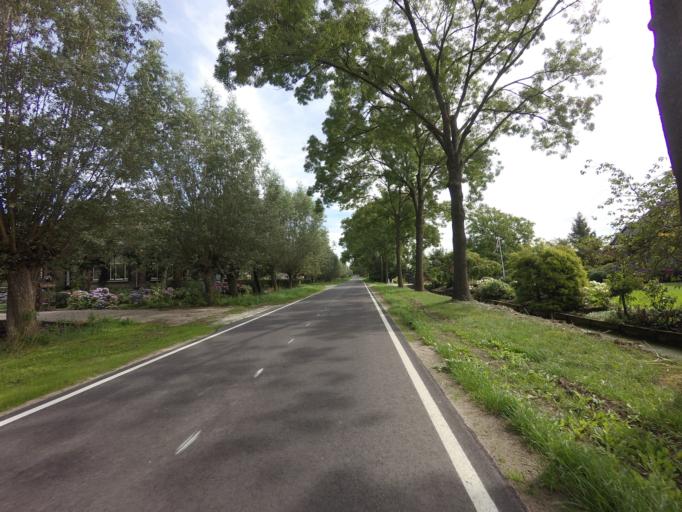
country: NL
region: Utrecht
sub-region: Stichtse Vecht
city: Spechtenkamp
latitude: 52.1215
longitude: 4.9647
